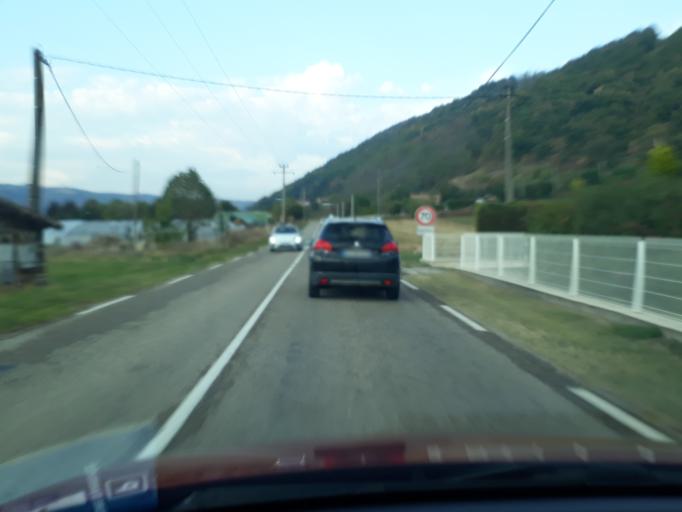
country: FR
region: Rhone-Alpes
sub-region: Departement du Rhone
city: Condrieu
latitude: 45.4629
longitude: 4.7882
